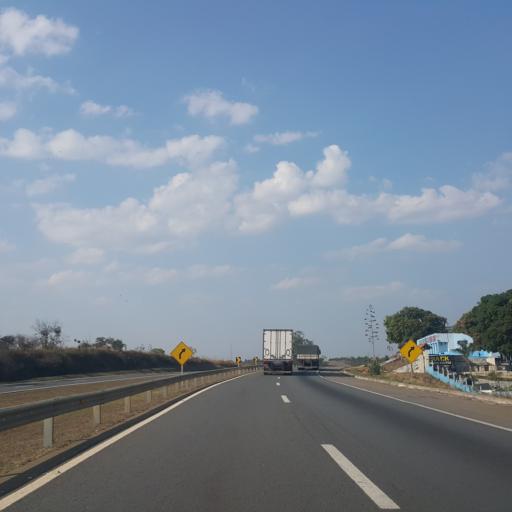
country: BR
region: Goias
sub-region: Abadiania
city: Abadiania
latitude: -16.1730
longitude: -48.6473
